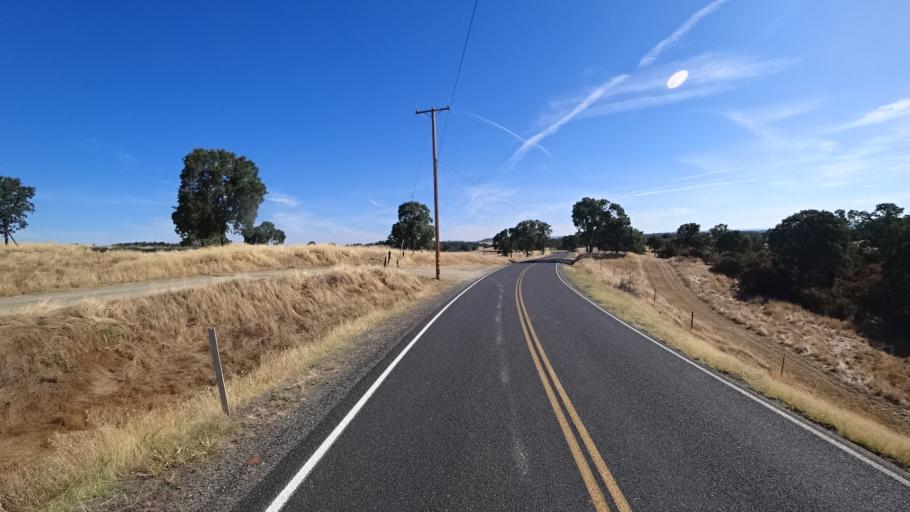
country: US
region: California
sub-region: Calaveras County
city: Valley Springs
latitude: 38.1667
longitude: -120.8143
